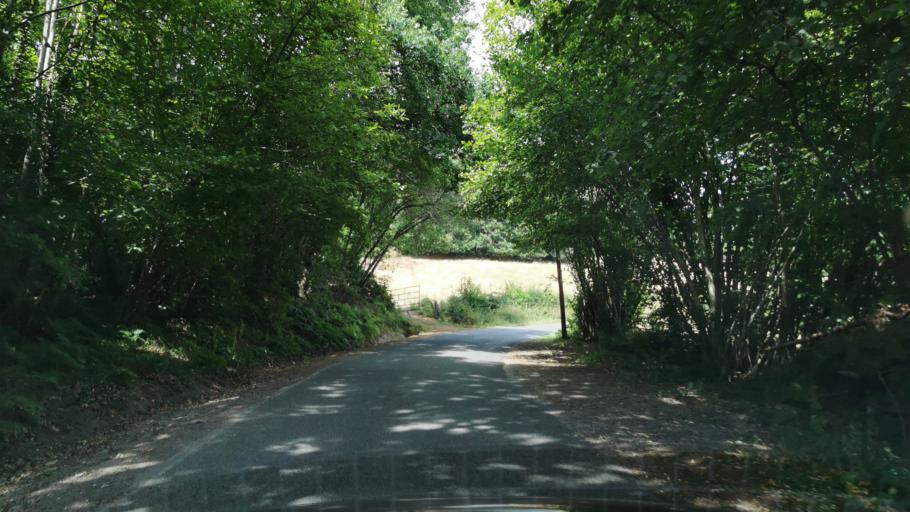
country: FR
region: Bourgogne
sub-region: Departement de Saone-et-Loire
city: Marmagne
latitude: 46.8063
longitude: 4.3062
